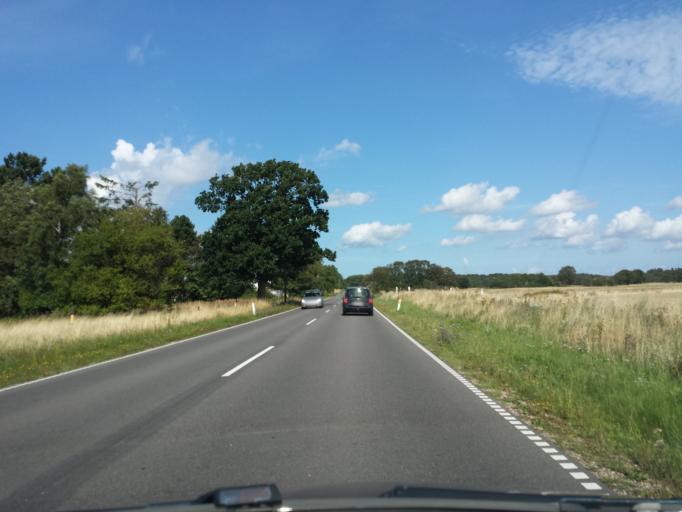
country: DK
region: Capital Region
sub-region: Frederikssund Kommune
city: Jaegerspris
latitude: 55.8851
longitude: 11.9552
